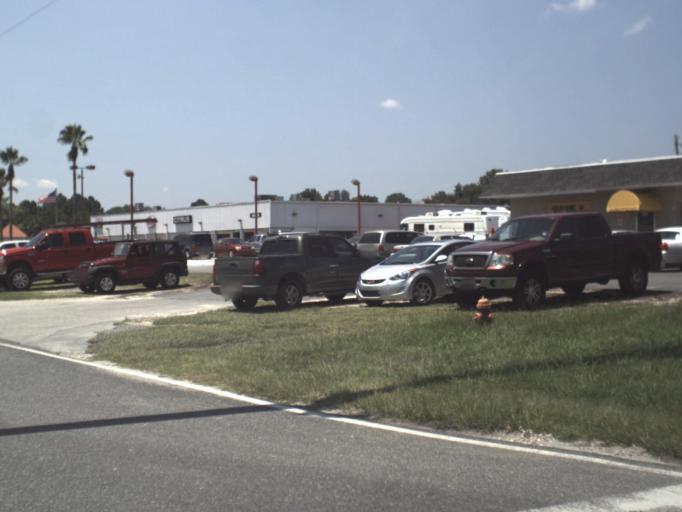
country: US
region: Florida
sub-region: Citrus County
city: Crystal River
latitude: 28.8823
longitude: -82.5826
